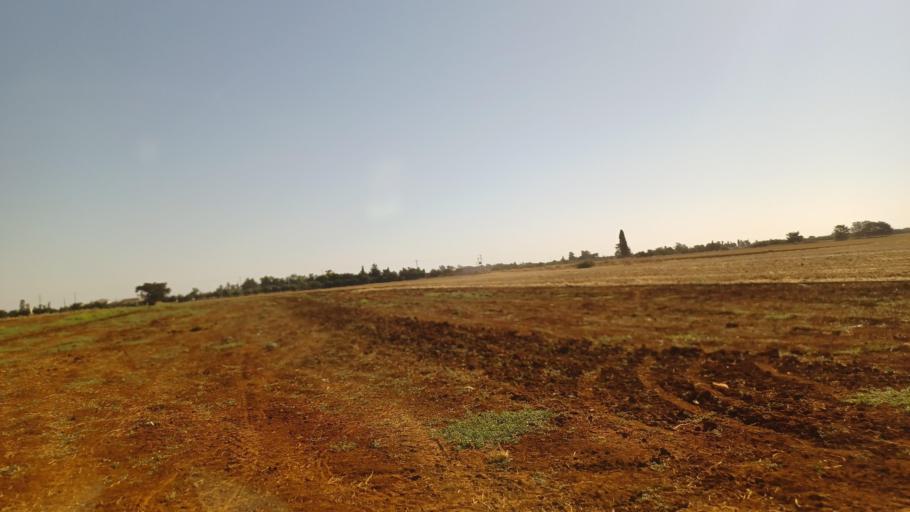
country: CY
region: Ammochostos
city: Avgorou
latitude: 35.0195
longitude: 33.8451
